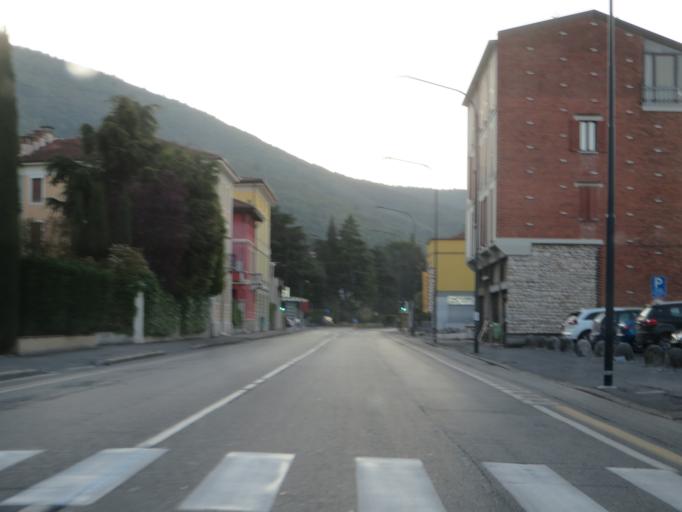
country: IT
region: Lombardy
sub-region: Provincia di Brescia
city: Brescia
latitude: 45.5313
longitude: 10.2479
